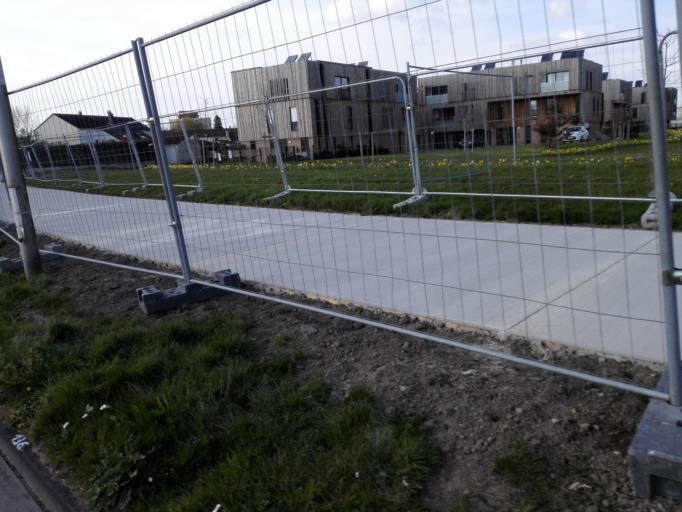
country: FR
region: Nord-Pas-de-Calais
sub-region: Departement du Nord
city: Grande-Synthe
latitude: 51.0042
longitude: 2.2921
